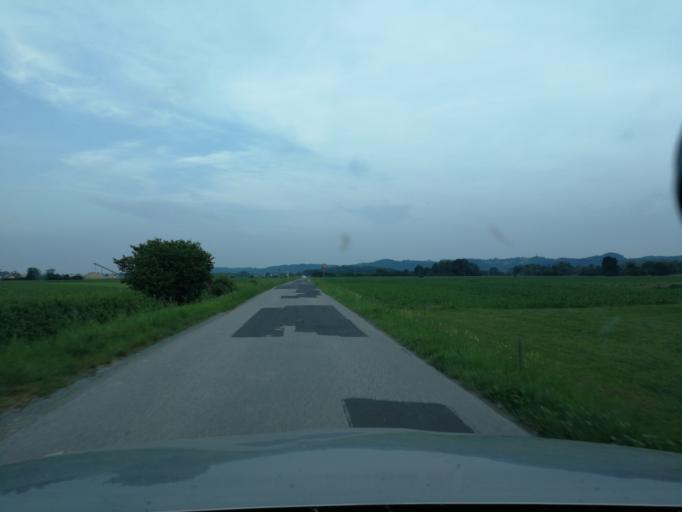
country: AT
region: Burgenland
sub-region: Politischer Bezirk Jennersdorf
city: Konigsdorf
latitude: 47.0199
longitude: 16.1481
